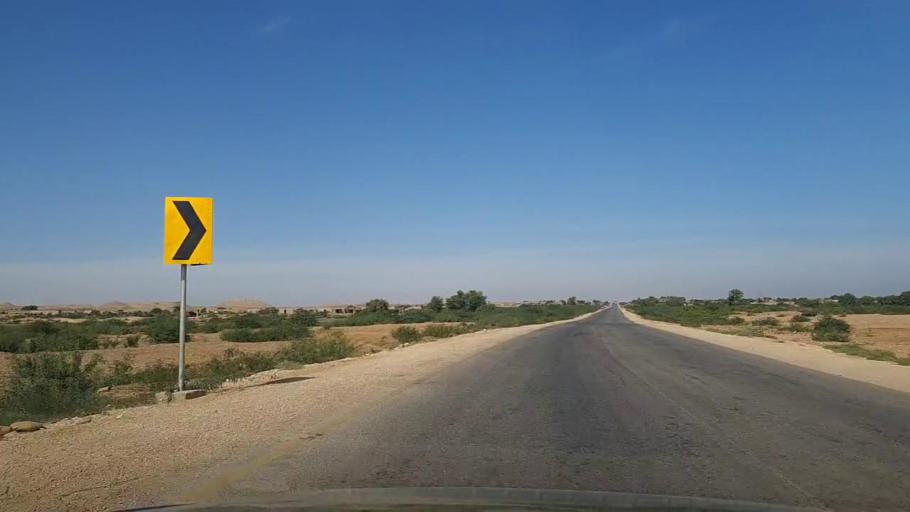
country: PK
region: Sindh
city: Kotri
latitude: 25.1743
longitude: 68.2397
